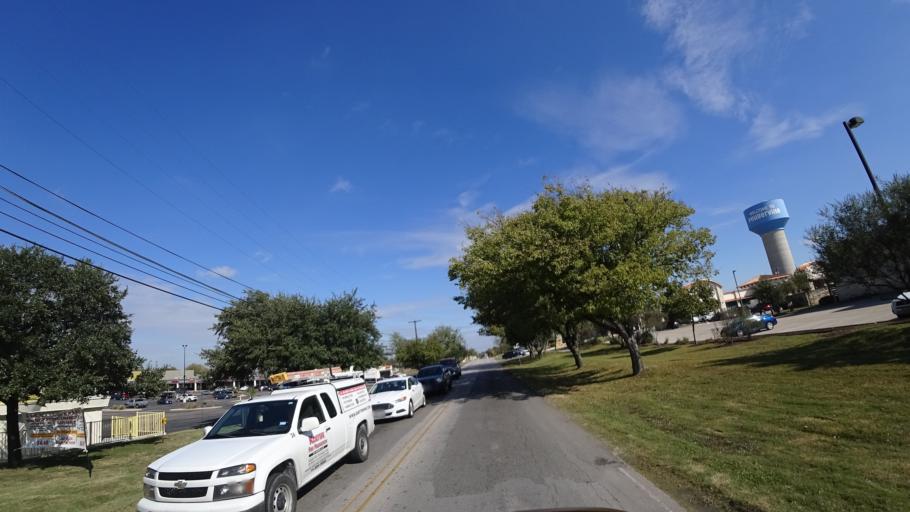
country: US
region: Texas
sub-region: Travis County
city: Windemere
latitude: 30.4490
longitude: -97.6559
